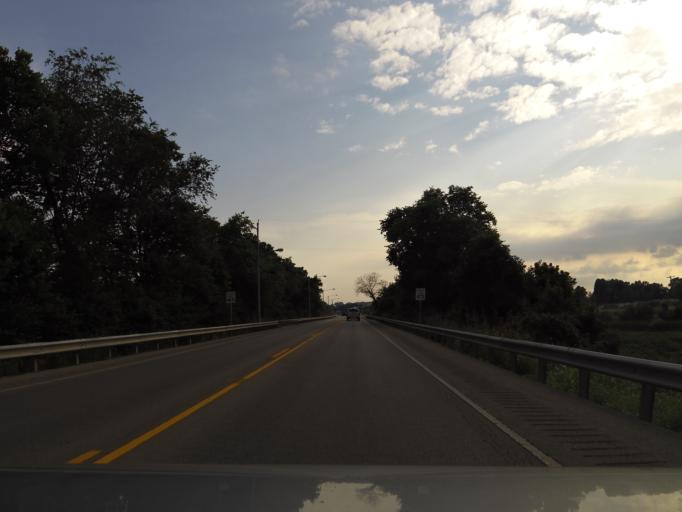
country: US
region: Kentucky
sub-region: Harrison County
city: Cynthiana
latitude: 38.3849
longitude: -84.3025
